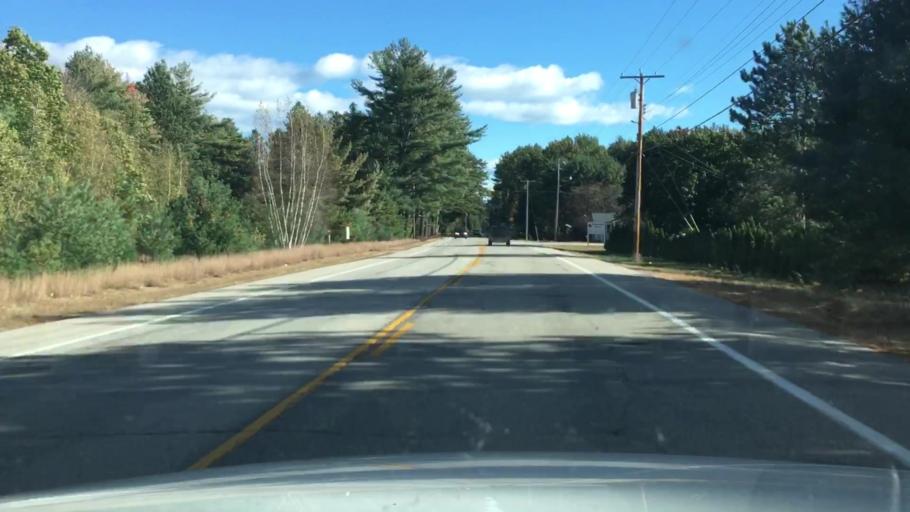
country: US
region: Maine
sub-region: York County
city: South Sanford
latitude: 43.3790
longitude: -70.6845
